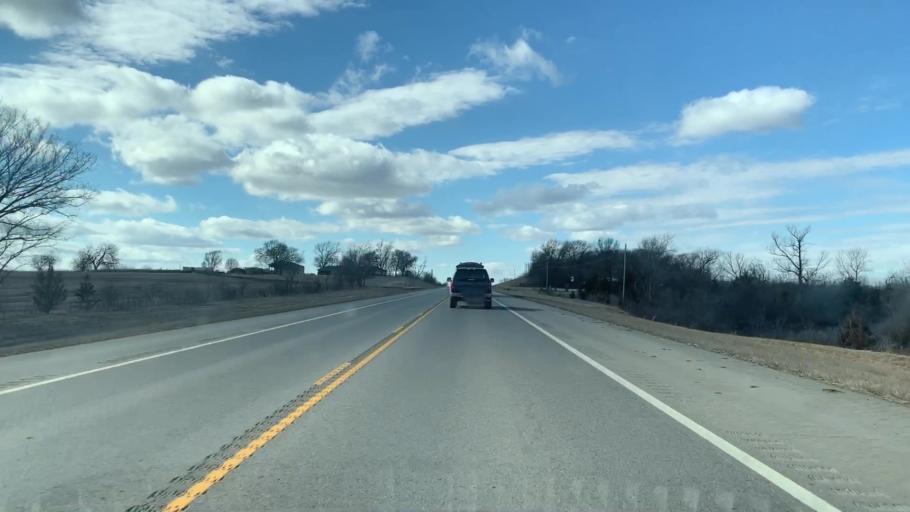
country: US
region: Kansas
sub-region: Cherokee County
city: Columbus
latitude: 37.3399
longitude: -94.8924
